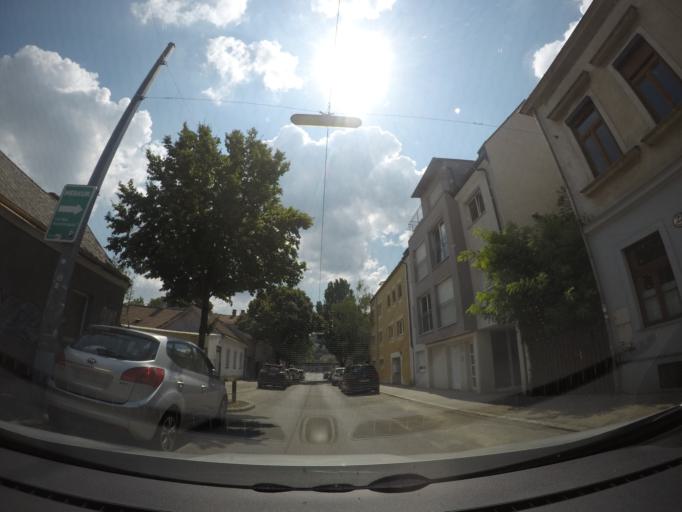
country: AT
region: Lower Austria
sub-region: Politischer Bezirk Modling
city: Perchtoldsdorf
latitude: 48.1986
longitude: 16.2627
